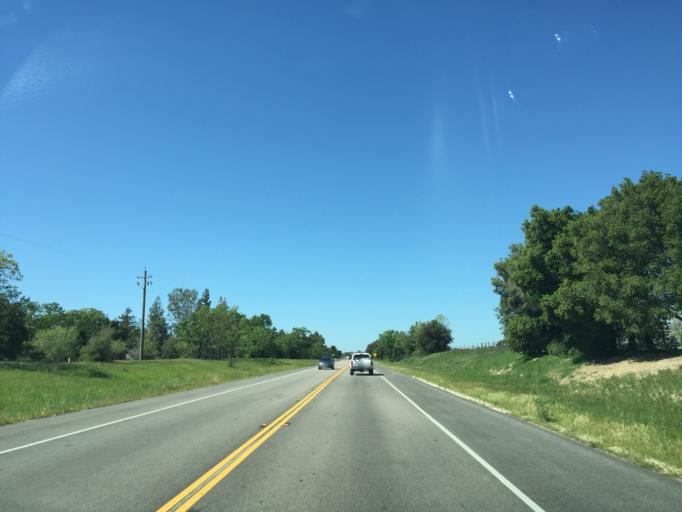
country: US
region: California
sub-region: Santa Barbara County
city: Los Olivos
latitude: 34.6543
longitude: -120.0985
